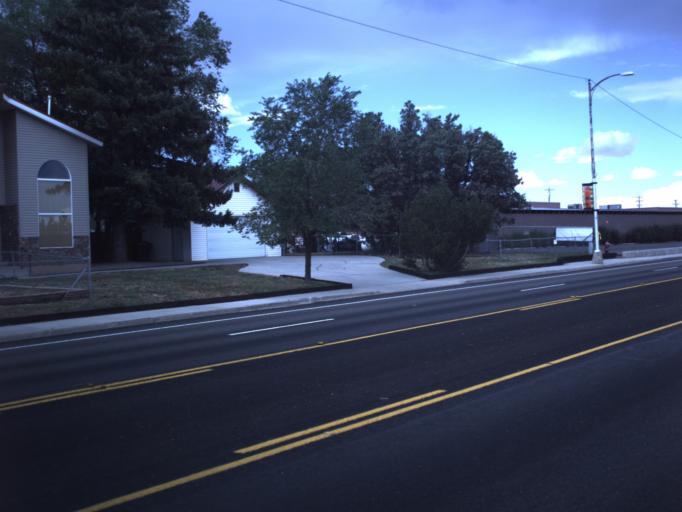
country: US
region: Utah
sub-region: San Juan County
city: Monticello
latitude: 37.8765
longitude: -109.3428
